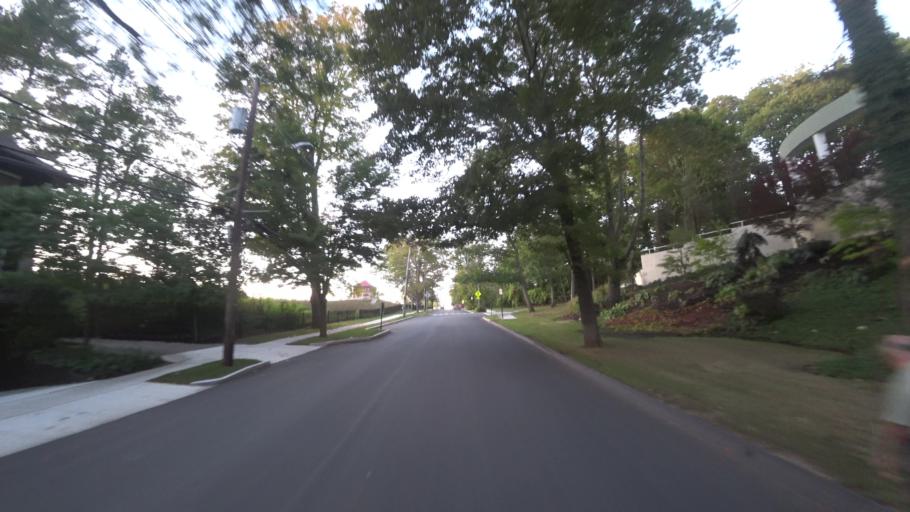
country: US
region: Massachusetts
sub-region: Norfolk County
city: Brookline
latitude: 42.3283
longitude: -71.1414
